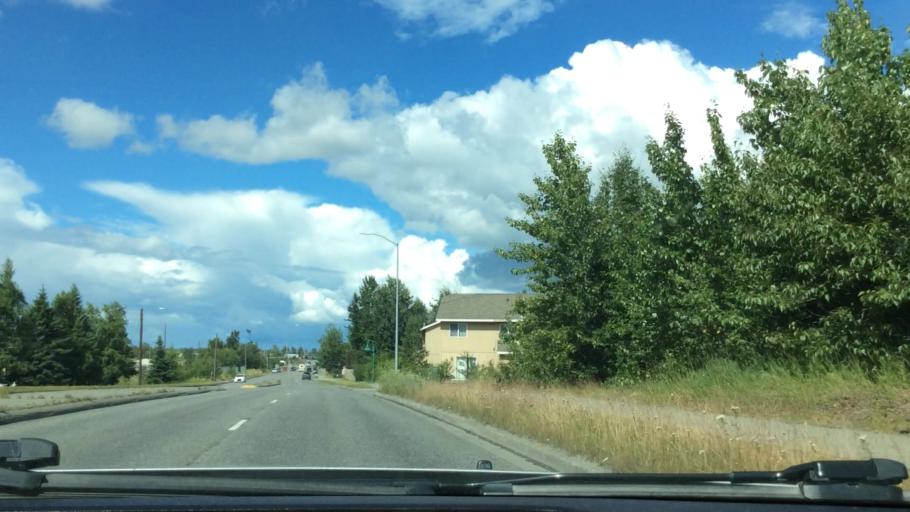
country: US
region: Alaska
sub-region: Anchorage Municipality
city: Anchorage
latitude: 61.2121
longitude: -149.8081
